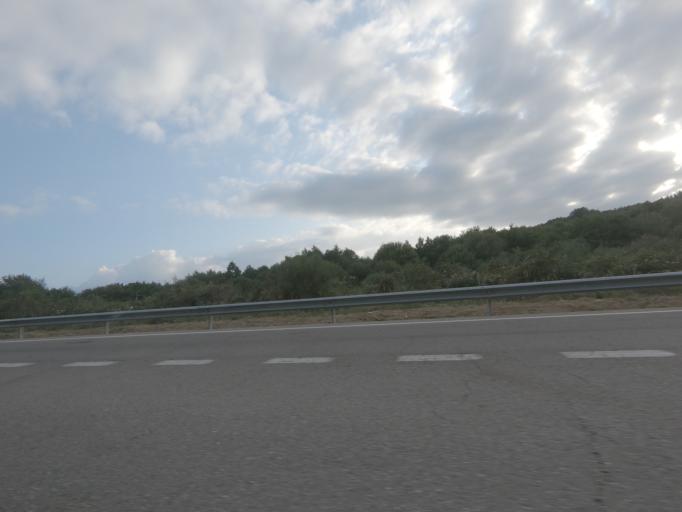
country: ES
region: Galicia
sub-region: Provincia de Ourense
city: Taboadela
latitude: 42.2220
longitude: -7.8426
